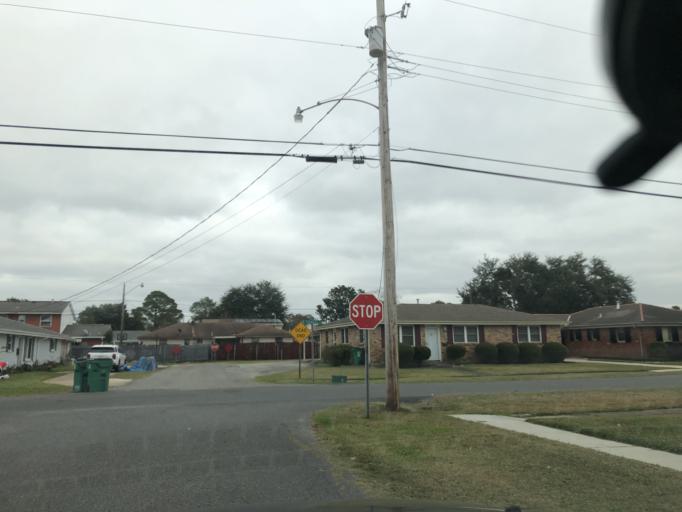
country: US
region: Louisiana
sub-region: Jefferson Parish
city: Metairie Terrace
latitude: 29.9864
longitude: -90.1679
